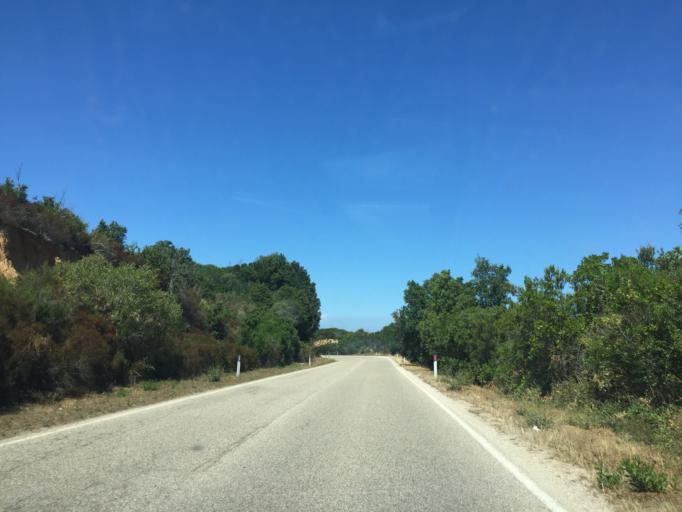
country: IT
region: Sardinia
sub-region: Provincia di Olbia-Tempio
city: Aglientu
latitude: 41.0873
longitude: 9.1182
